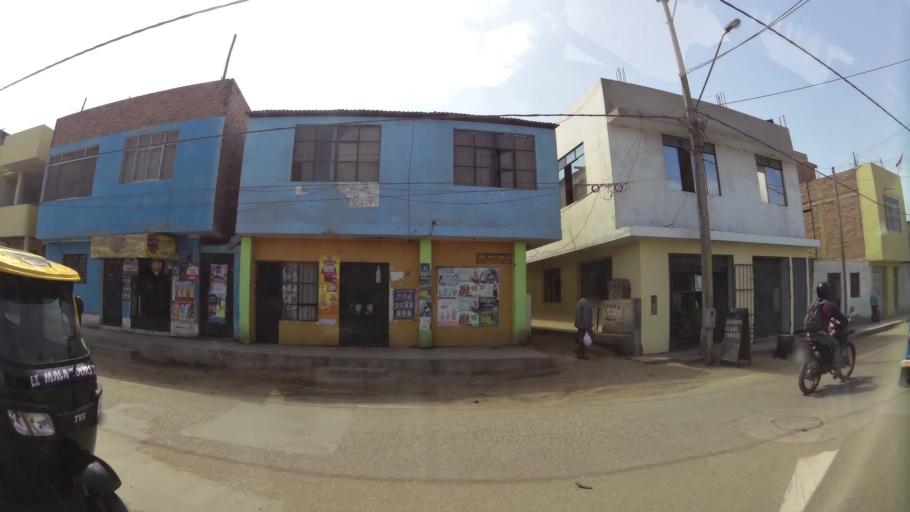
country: PE
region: Lima
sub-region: Provincia de Canete
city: Mala
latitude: -12.6544
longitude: -76.6327
